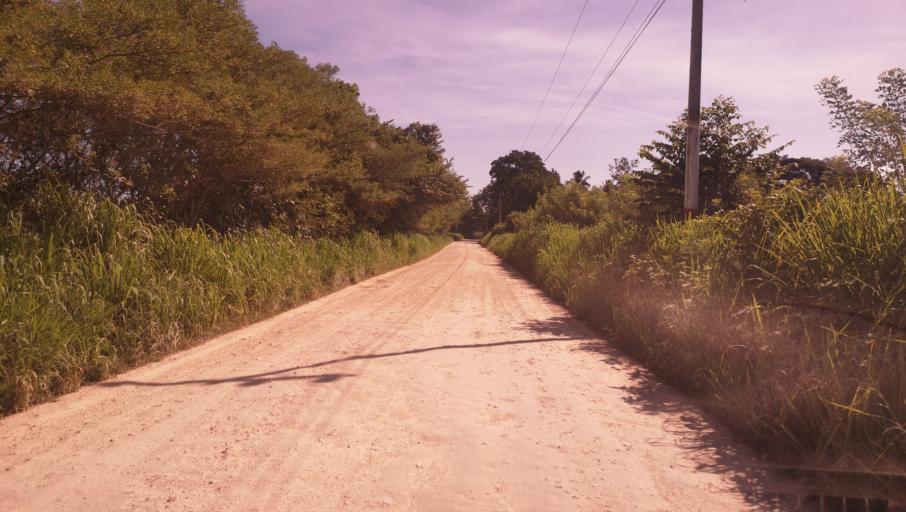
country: GT
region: Peten
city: Dolores
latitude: 16.7205
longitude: -89.3602
